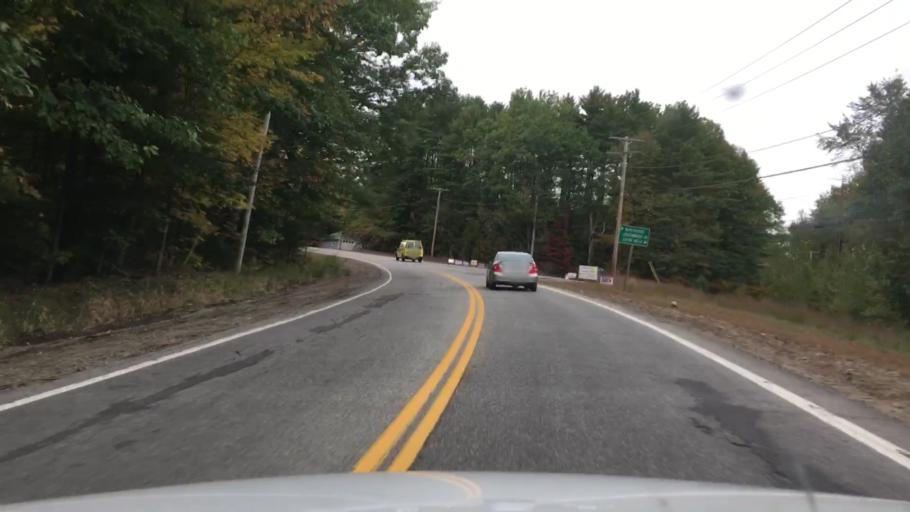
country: US
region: Maine
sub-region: Oxford County
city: Norway
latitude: 44.2215
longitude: -70.5894
